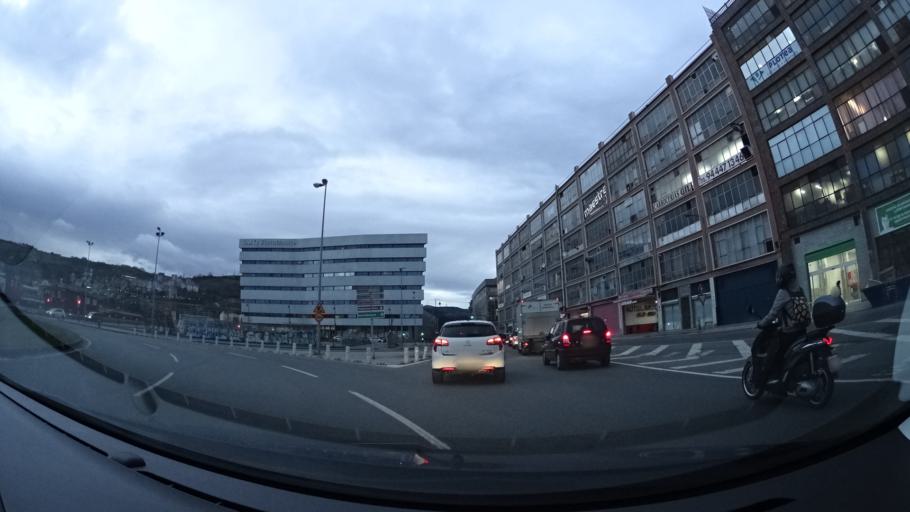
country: ES
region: Basque Country
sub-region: Bizkaia
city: Bilbao
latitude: 43.2679
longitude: -2.9501
